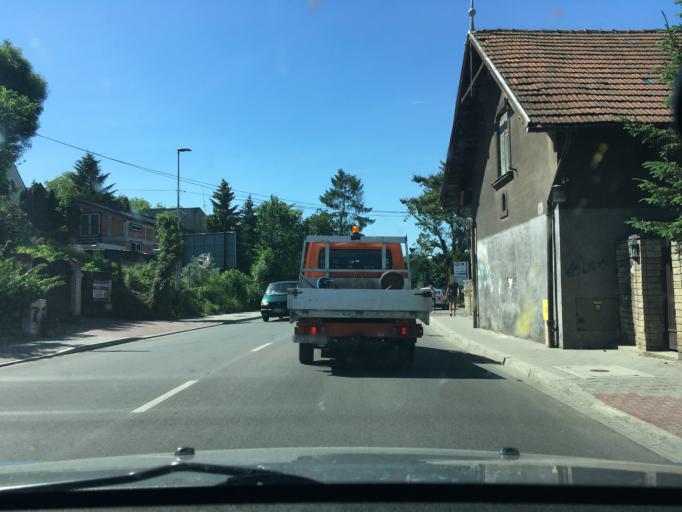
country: PL
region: Lesser Poland Voivodeship
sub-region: Krakow
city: Krakow
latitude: 50.0572
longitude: 19.9009
